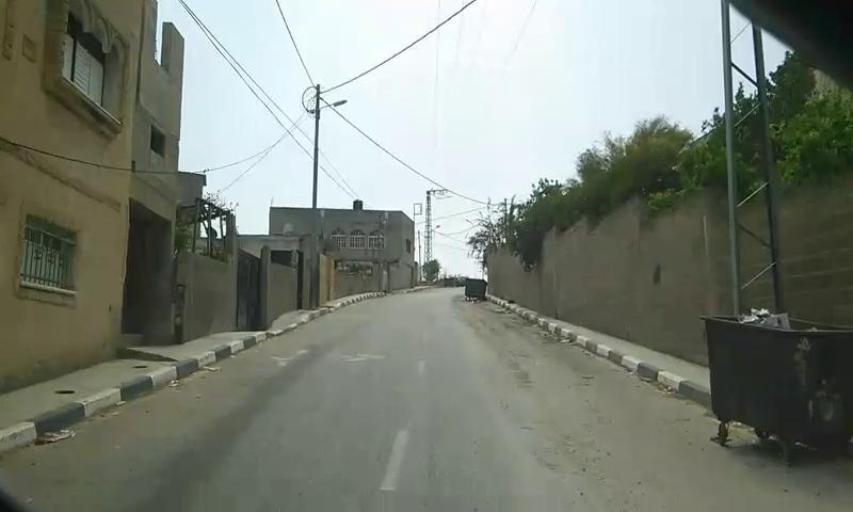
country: PS
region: West Bank
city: Silat al Harithiyah
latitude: 32.5222
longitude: 35.2226
